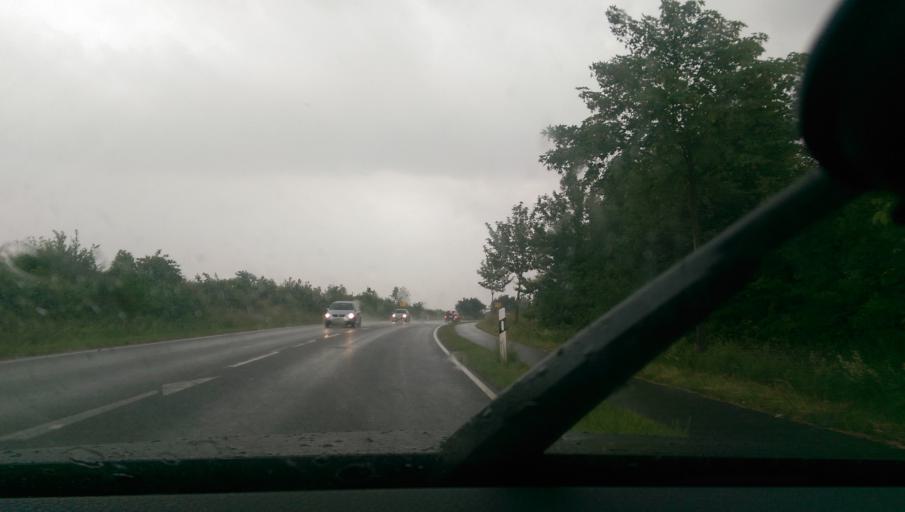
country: DE
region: Lower Saxony
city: Erkerode
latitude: 52.2496
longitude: 10.7322
